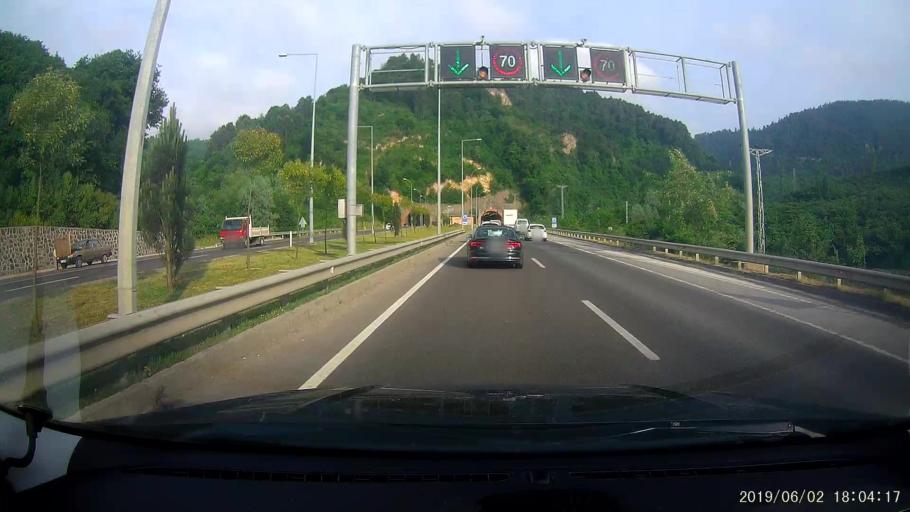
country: TR
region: Ordu
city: Unieh
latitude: 41.1215
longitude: 37.2288
